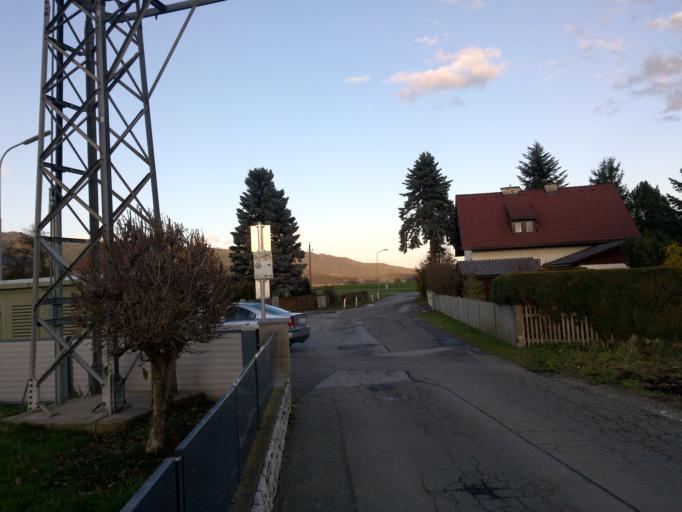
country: AT
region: Styria
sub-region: Politischer Bezirk Murtal
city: Fohnsdorf
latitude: 47.1960
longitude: 14.7133
